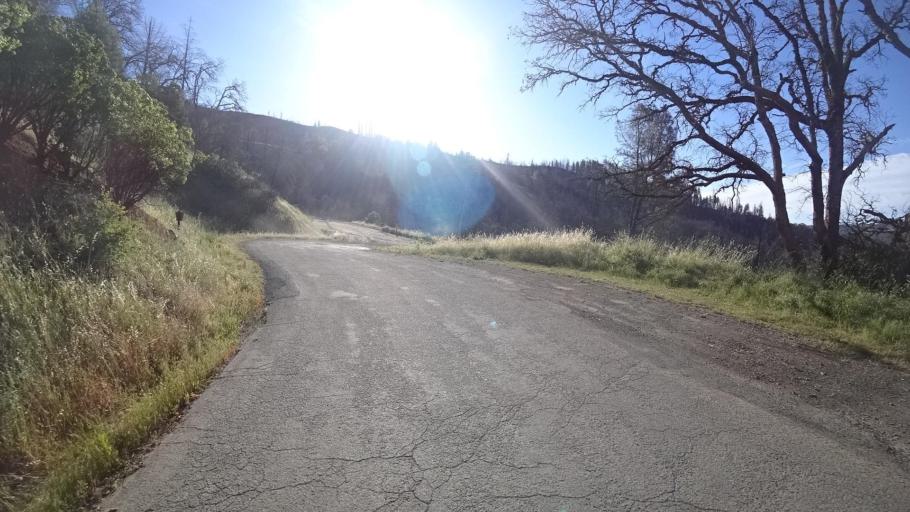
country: US
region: California
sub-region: Lake County
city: Upper Lake
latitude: 39.2723
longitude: -122.9240
